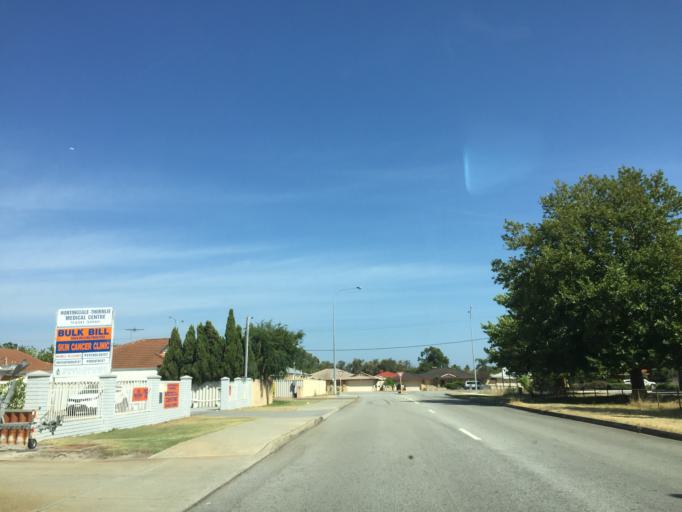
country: AU
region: Western Australia
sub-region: Gosnells
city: Thornlie
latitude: -32.0789
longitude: 115.9581
